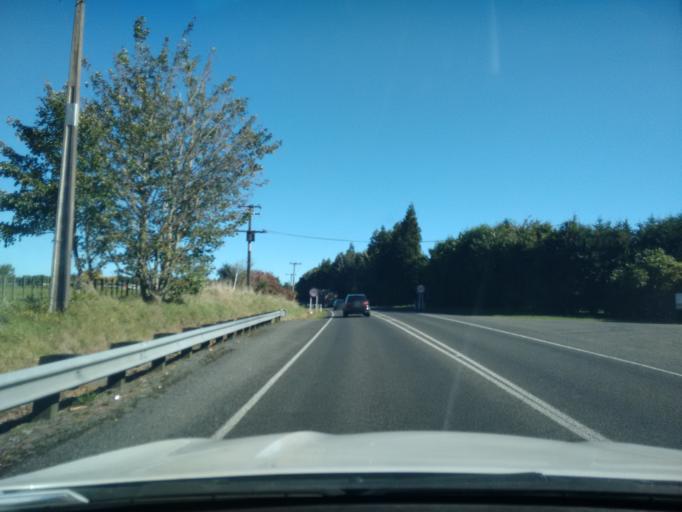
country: NZ
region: Taranaki
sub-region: New Plymouth District
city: New Plymouth
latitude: -39.1536
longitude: 174.1897
